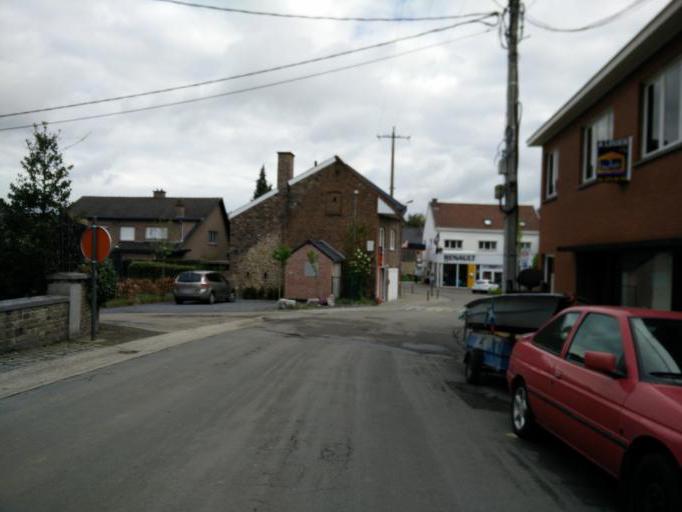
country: NL
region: Limburg
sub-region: Eijsden-Margraten
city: Eijsden
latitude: 50.7583
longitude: 5.7606
